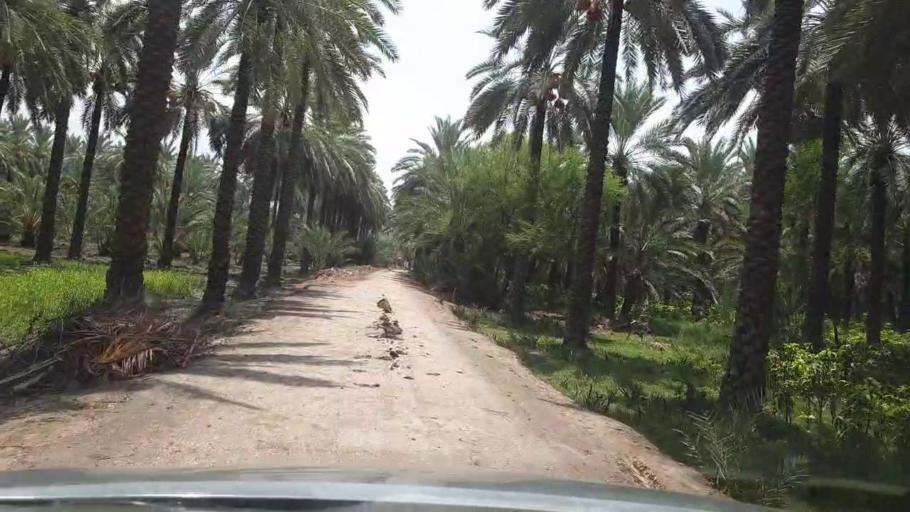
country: PK
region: Sindh
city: Khairpur
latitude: 27.6344
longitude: 68.7318
